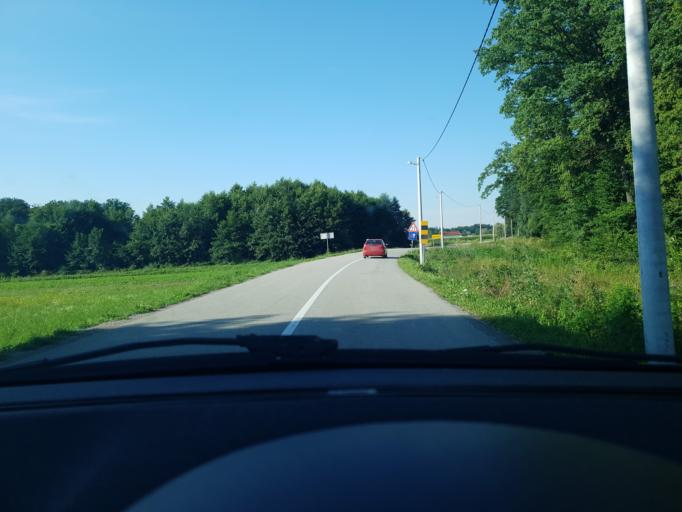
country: HR
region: Zagrebacka
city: Jakovlje
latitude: 45.9558
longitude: 15.8520
